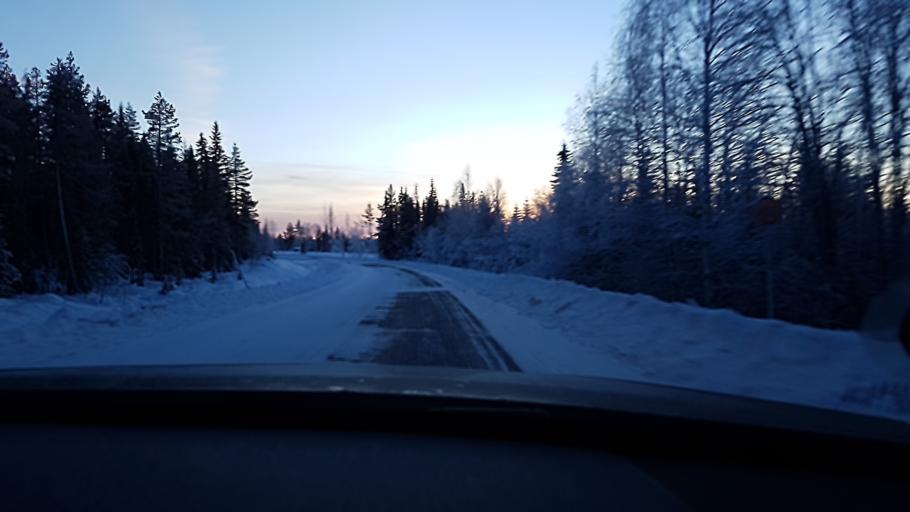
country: SE
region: Vaesterbotten
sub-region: Storumans Kommun
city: Storuman
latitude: 65.1531
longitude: 17.2596
